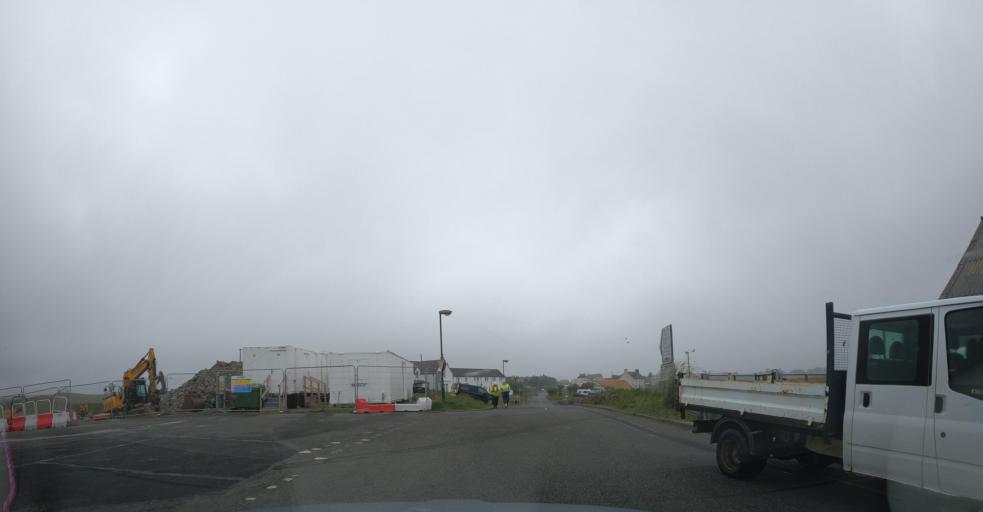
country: GB
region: Scotland
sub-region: Eilean Siar
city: Isle of North Uist
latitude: 57.5974
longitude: -7.1578
